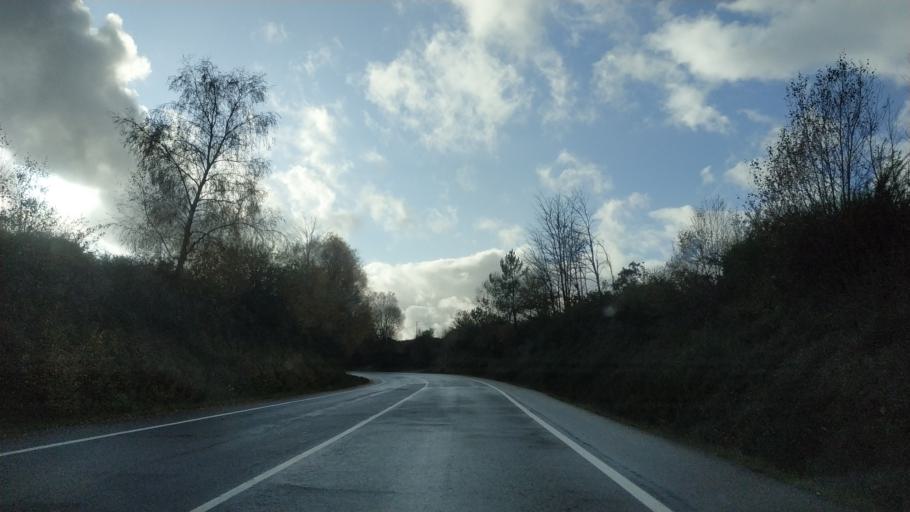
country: ES
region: Galicia
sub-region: Provincia da Coruna
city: Arzua
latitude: 42.9590
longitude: -8.1517
